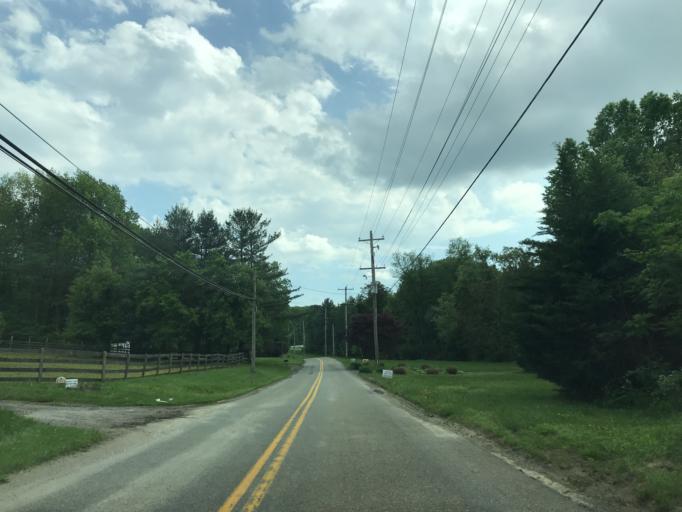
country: US
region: Pennsylvania
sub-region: York County
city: Susquehanna Trails
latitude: 39.6994
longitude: -76.3624
